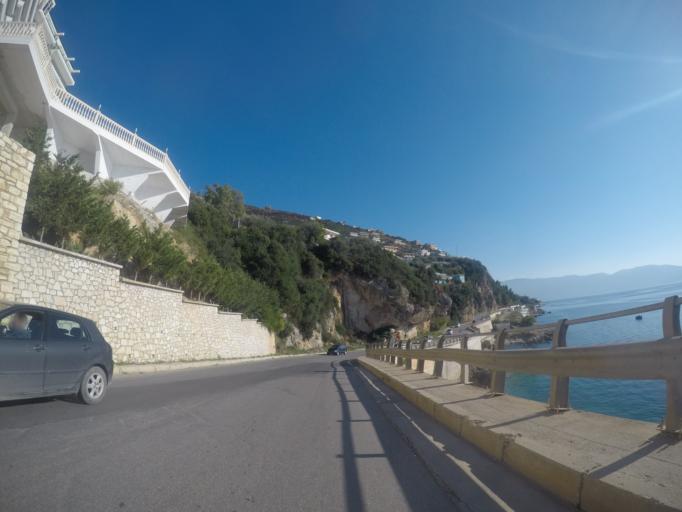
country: AL
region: Vlore
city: Vlore
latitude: 40.4130
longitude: 19.4809
